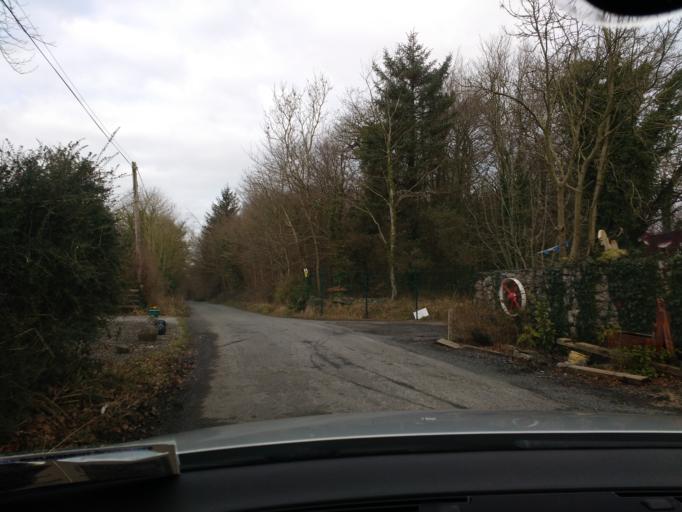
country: IE
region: Leinster
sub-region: Laois
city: Rathdowney
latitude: 52.6628
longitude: -7.5593
